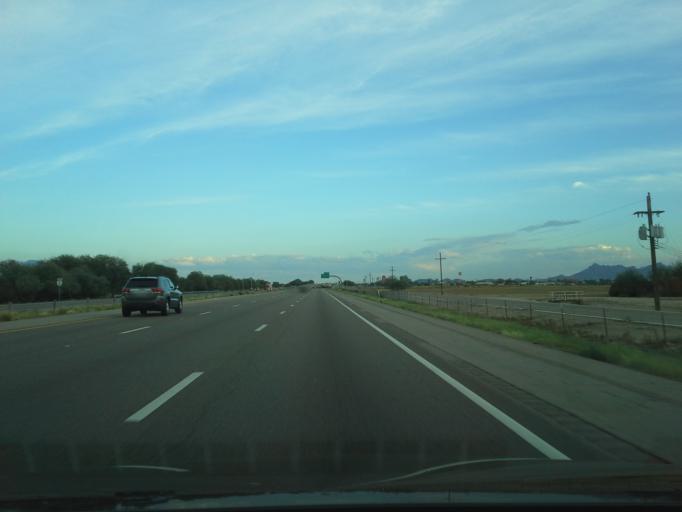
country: US
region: Arizona
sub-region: Pima County
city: Marana
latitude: 32.4687
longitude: -111.2259
